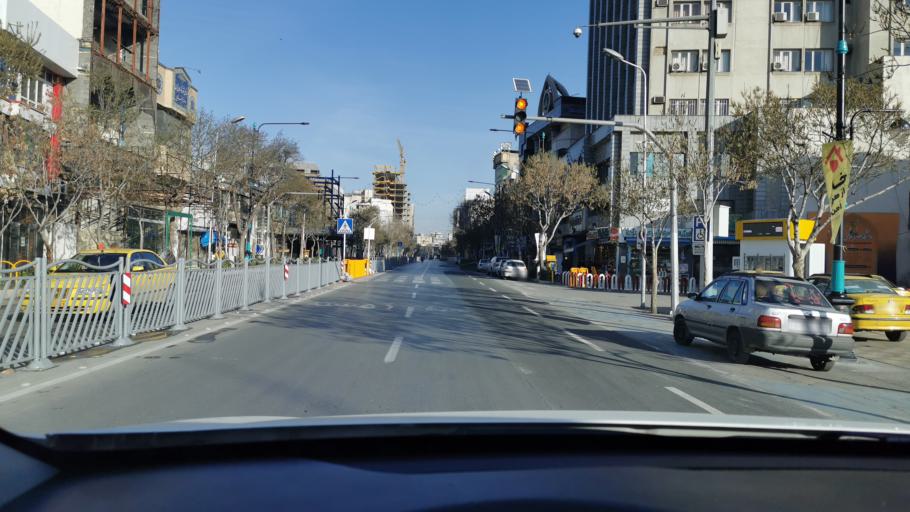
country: IR
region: Razavi Khorasan
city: Mashhad
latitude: 36.2861
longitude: 59.6104
